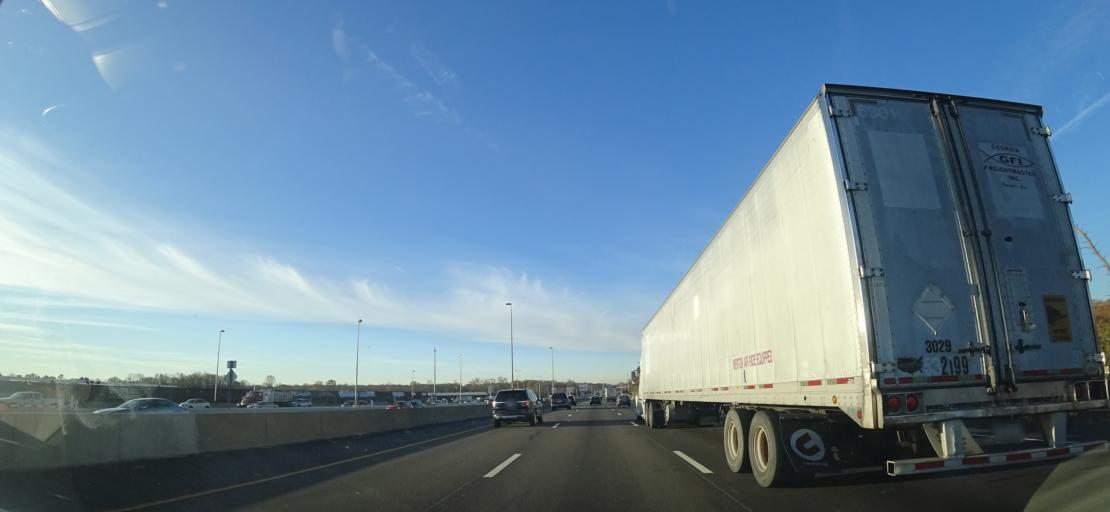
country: US
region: Virginia
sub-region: Fairfax County
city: Newington
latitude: 38.7304
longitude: -77.1984
